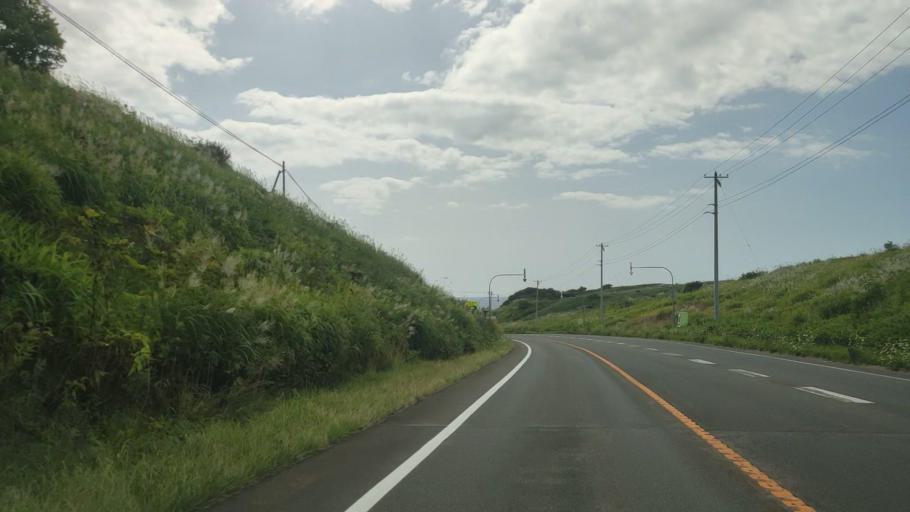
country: JP
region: Hokkaido
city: Rumoi
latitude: 44.5501
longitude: 141.7719
